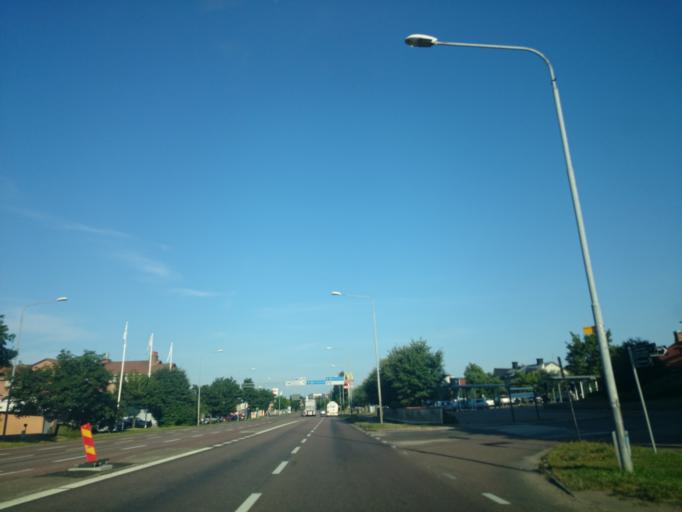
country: SE
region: Vaesternorrland
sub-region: Sundsvalls Kommun
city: Sundsvall
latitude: 62.3878
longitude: 17.3148
